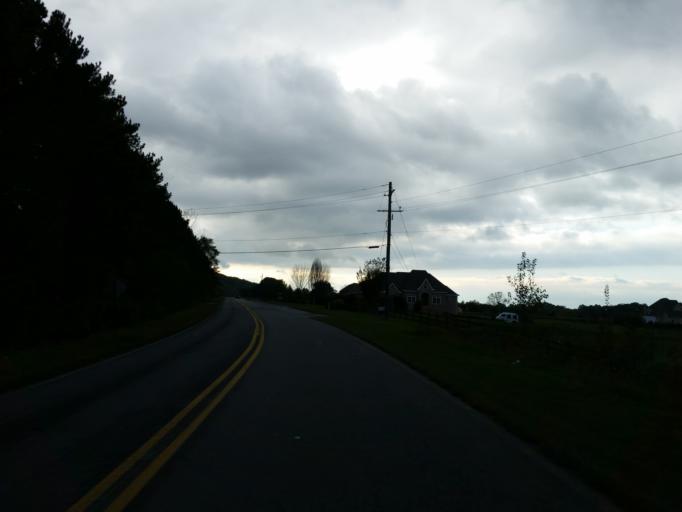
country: US
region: Georgia
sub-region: Bartow County
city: Emerson
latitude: 34.1175
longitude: -84.7994
